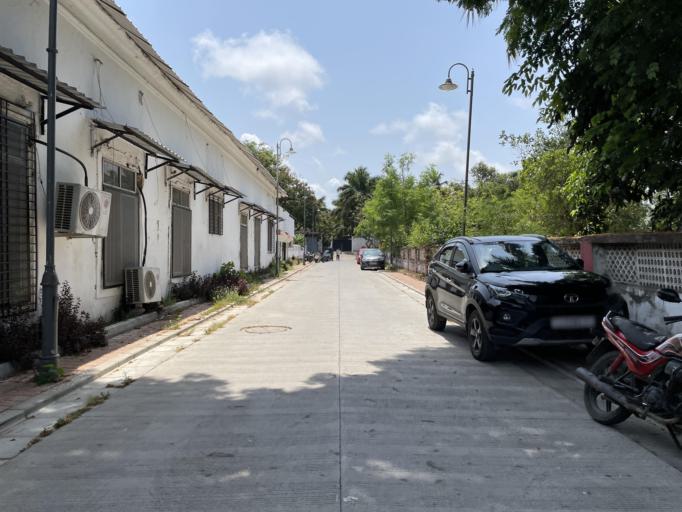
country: IN
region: Daman and Diu
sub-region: Daman District
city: Daman
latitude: 20.4080
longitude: 72.8322
